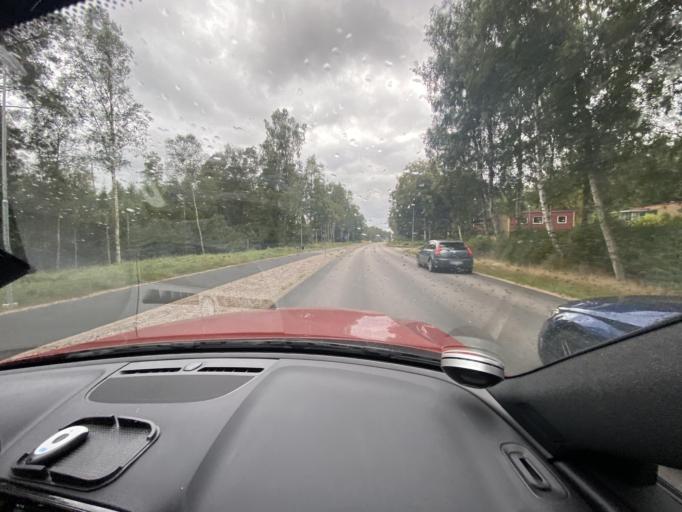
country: SE
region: Kronoberg
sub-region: Markaryds Kommun
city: Markaryd
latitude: 56.4540
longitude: 13.6160
